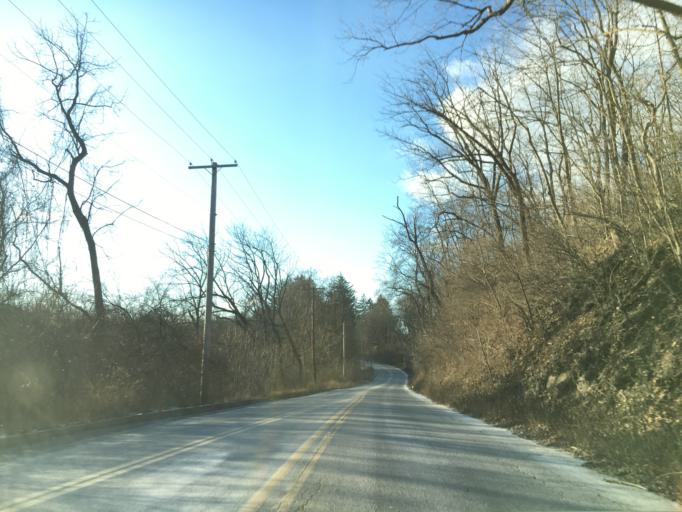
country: US
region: Pennsylvania
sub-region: Lehigh County
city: Egypt
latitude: 40.6735
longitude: -75.5187
